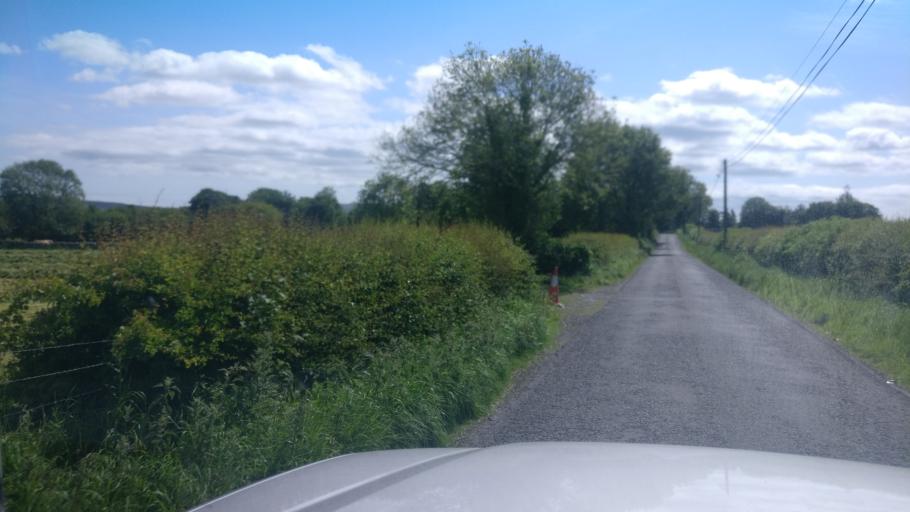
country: IE
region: Connaught
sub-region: County Galway
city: Gort
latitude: 53.1525
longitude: -8.7502
